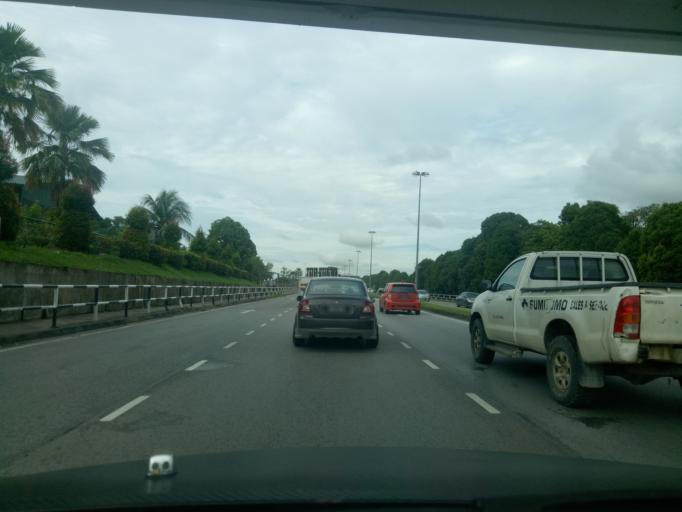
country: MY
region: Sarawak
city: Kuching
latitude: 1.5464
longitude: 110.3823
